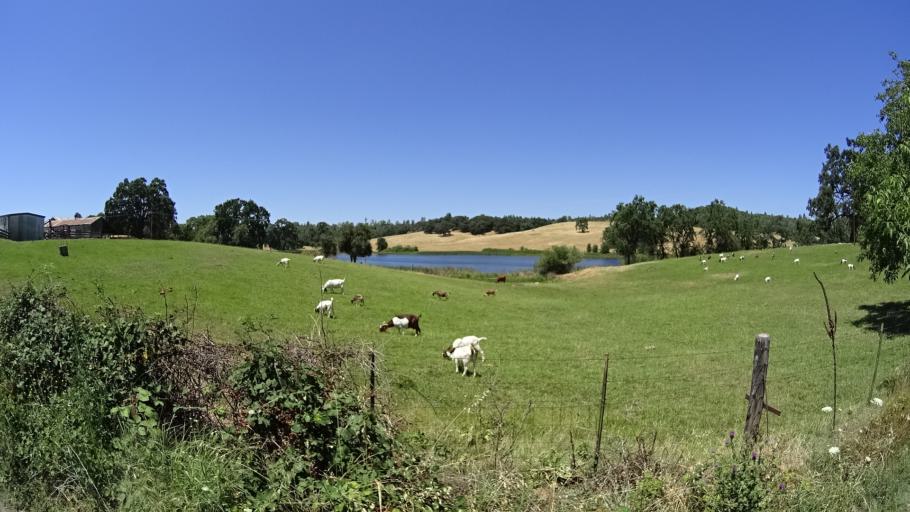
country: US
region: California
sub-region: Calaveras County
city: Angels Camp
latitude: 38.1155
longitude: -120.5125
